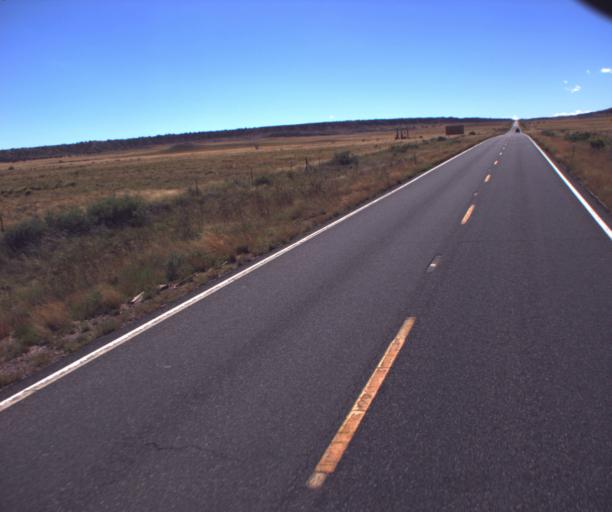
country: US
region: Arizona
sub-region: Apache County
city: Saint Johns
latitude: 34.6764
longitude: -109.2848
